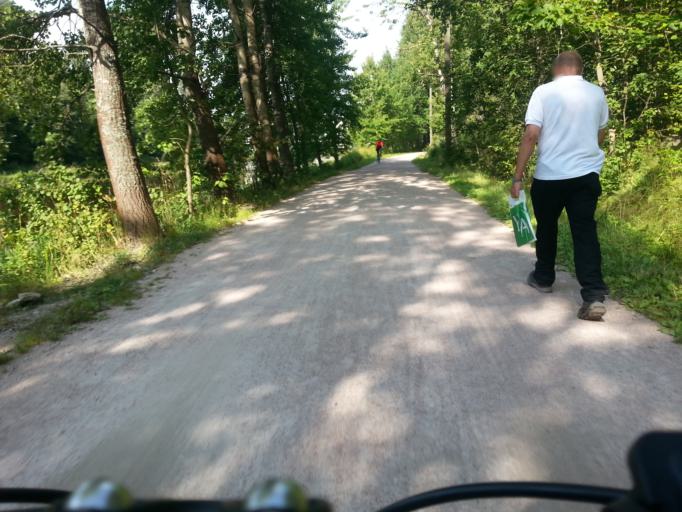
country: FI
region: Uusimaa
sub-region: Helsinki
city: Helsinki
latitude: 60.2292
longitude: 24.9883
